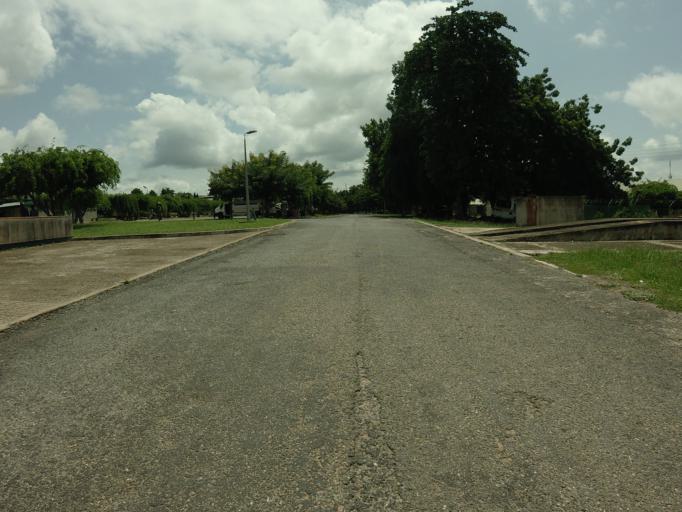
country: GH
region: Volta
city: Ho
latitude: 6.6005
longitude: 0.4848
